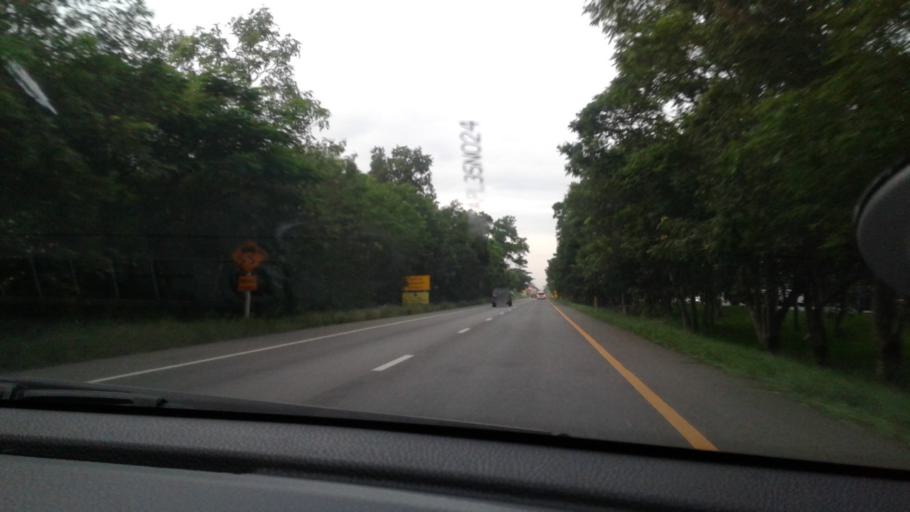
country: TH
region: Prachuap Khiri Khan
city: Pran Buri
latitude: 12.4792
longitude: 99.8929
